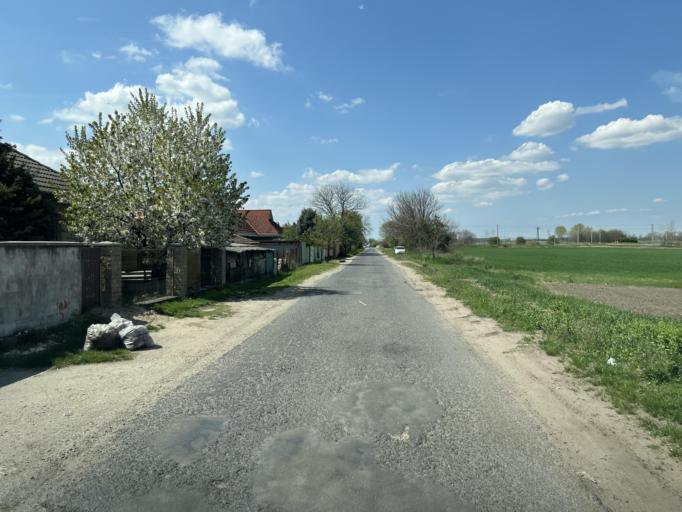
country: HU
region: Pest
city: Gyal
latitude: 47.3868
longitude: 19.2429
